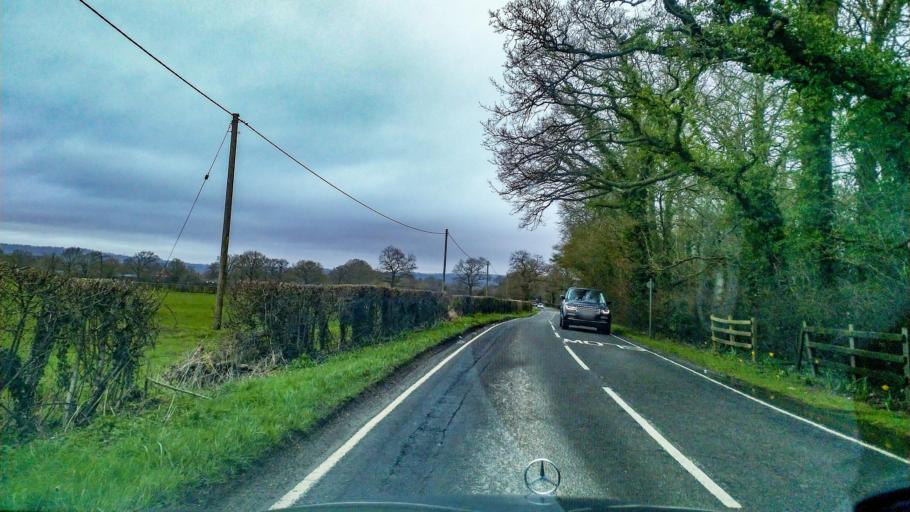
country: GB
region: England
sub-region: Surrey
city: Newdigate
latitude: 51.1986
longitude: -0.2467
